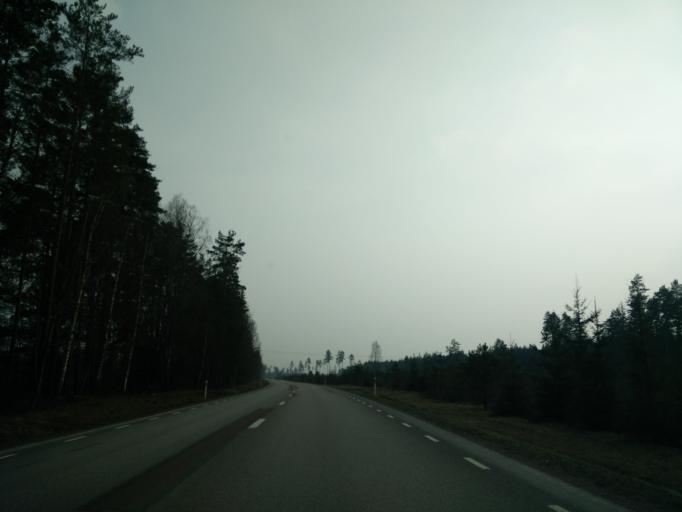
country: SE
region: Vaermland
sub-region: Forshaga Kommun
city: Forshaga
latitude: 59.5086
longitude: 13.4370
